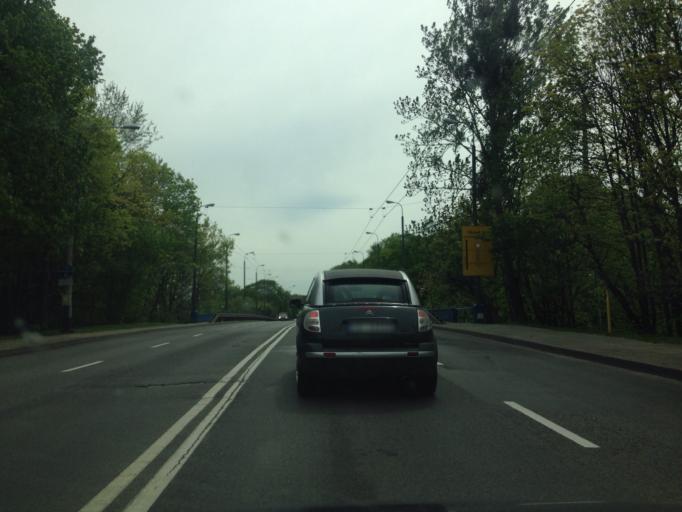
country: PL
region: Pomeranian Voivodeship
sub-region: Sopot
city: Sopot
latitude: 54.4545
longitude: 18.5558
